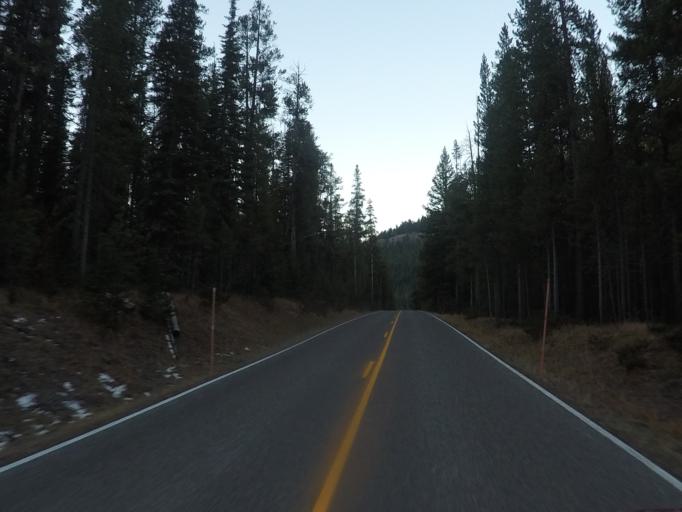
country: US
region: Montana
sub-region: Stillwater County
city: Absarokee
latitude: 44.9489
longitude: -110.0788
